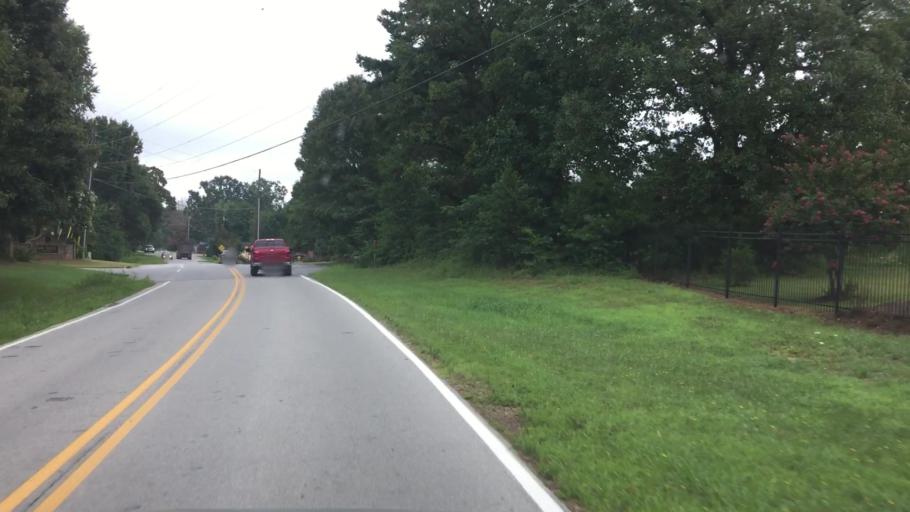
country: US
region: Georgia
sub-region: Barrow County
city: Winder
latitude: 34.0290
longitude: -83.7341
